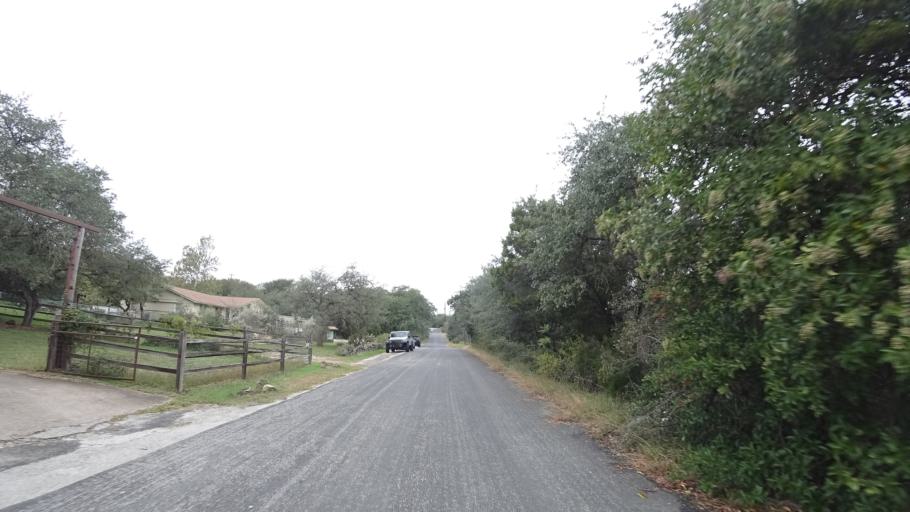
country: US
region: Texas
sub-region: Travis County
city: Barton Creek
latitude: 30.2325
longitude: -97.8994
